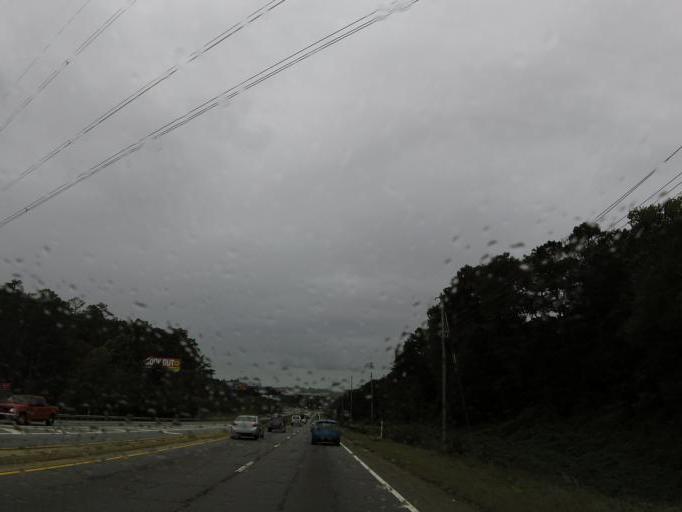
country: US
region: Georgia
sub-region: Cobb County
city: Kennesaw
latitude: 33.9940
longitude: -84.5816
